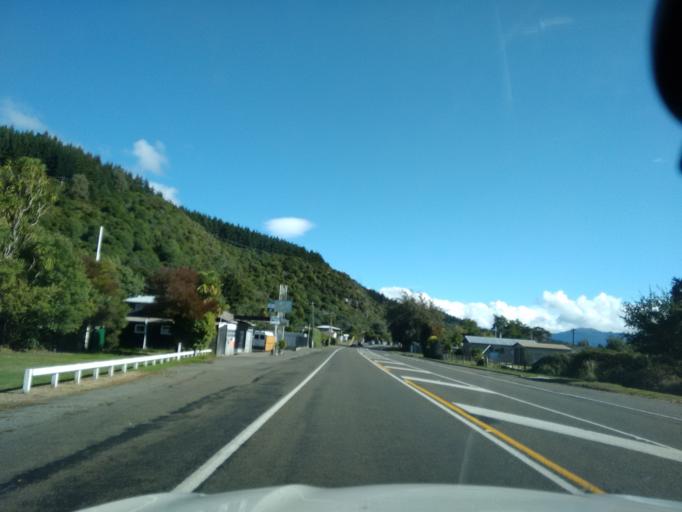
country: NZ
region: Waikato
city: Turangi
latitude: -38.9314
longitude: 175.8766
